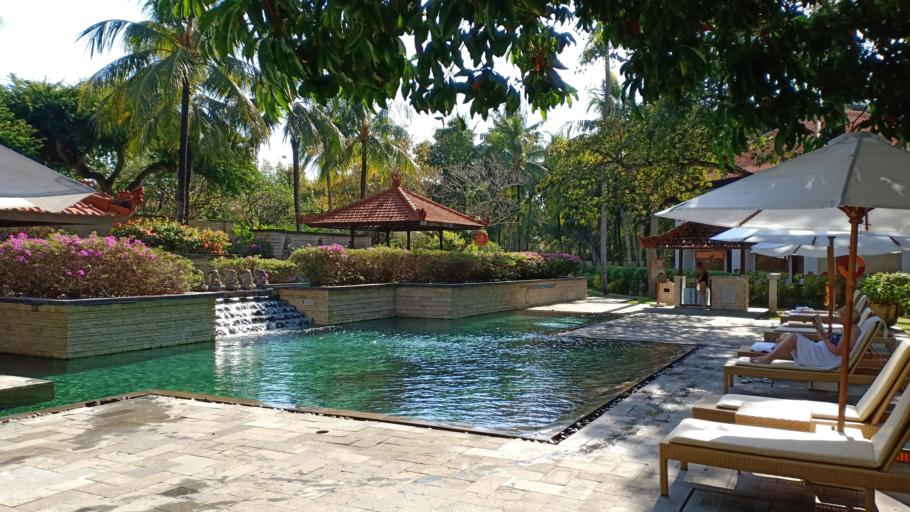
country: ID
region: Bali
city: Bualu
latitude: -8.8027
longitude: 115.2331
